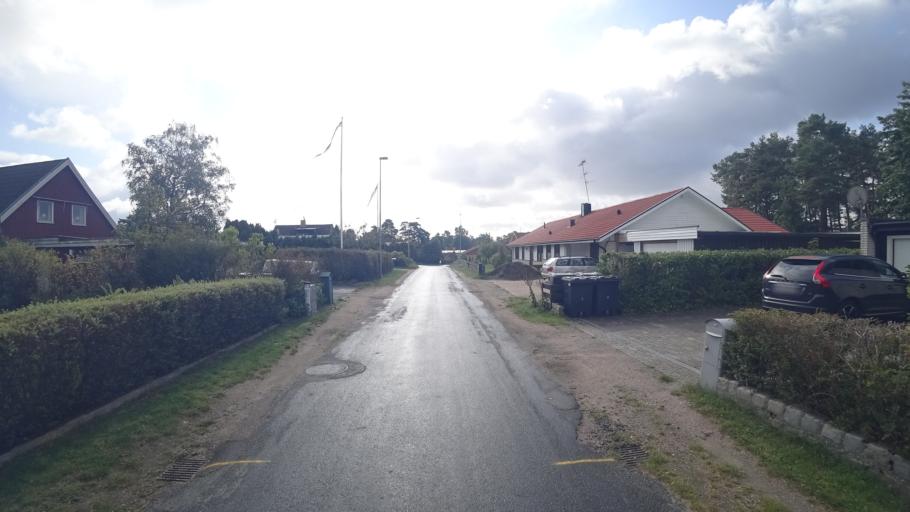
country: SE
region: Skane
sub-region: Kristianstads Kommun
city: Ahus
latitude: 55.9353
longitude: 14.3028
